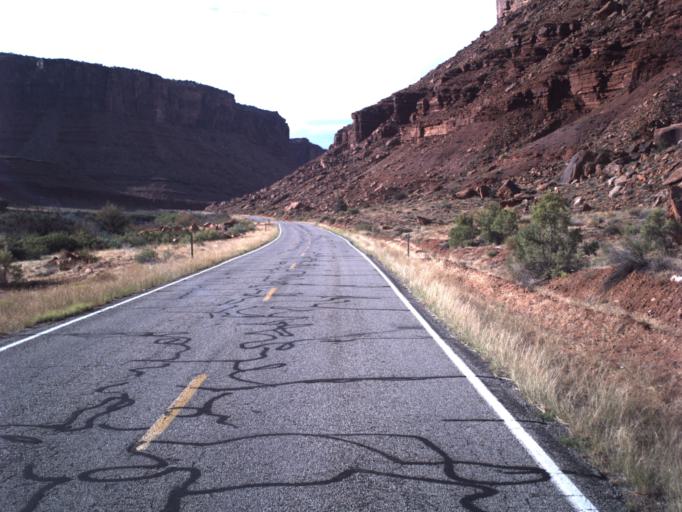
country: US
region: Utah
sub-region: Grand County
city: Moab
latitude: 38.7708
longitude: -109.3230
